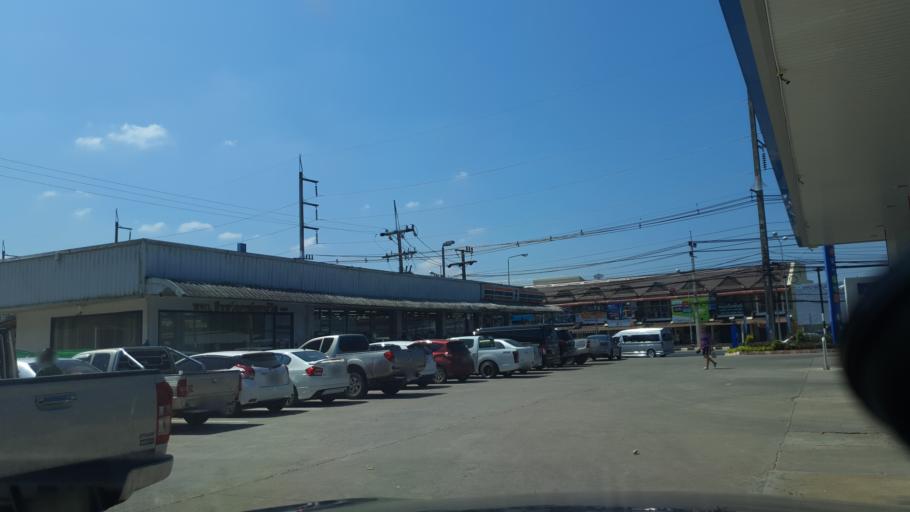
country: TH
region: Krabi
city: Khlong Thom
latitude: 7.9419
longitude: 99.1450
